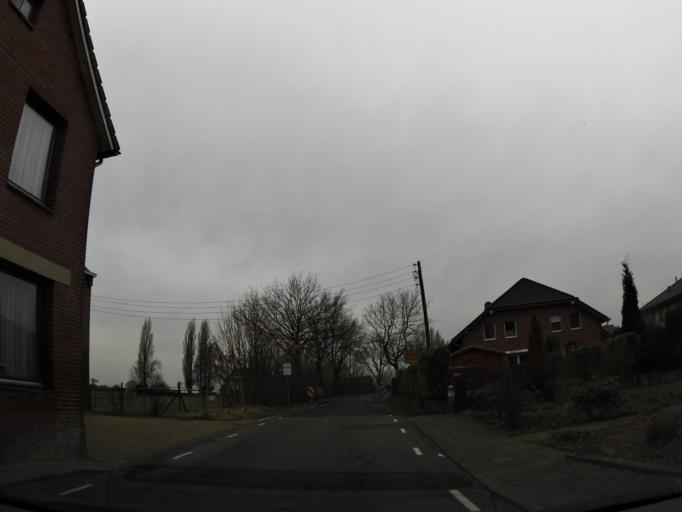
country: NL
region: Limburg
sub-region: Gemeente Schinnen
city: Doenrade
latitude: 50.9756
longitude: 5.9094
